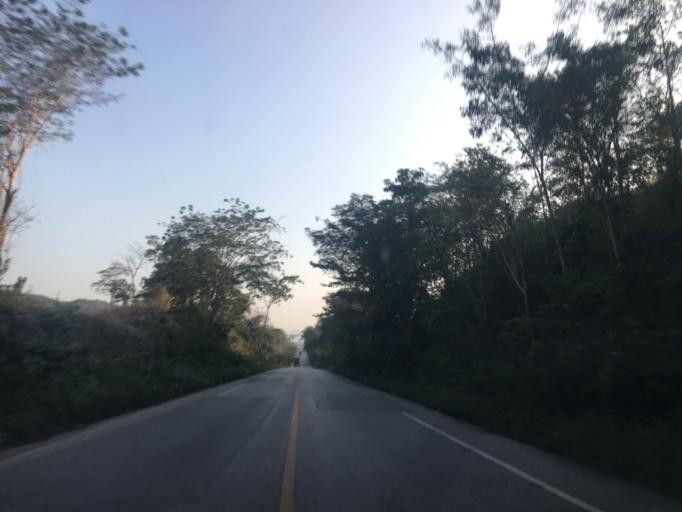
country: TH
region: Lampang
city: Ngao
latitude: 18.6563
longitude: 100.0177
